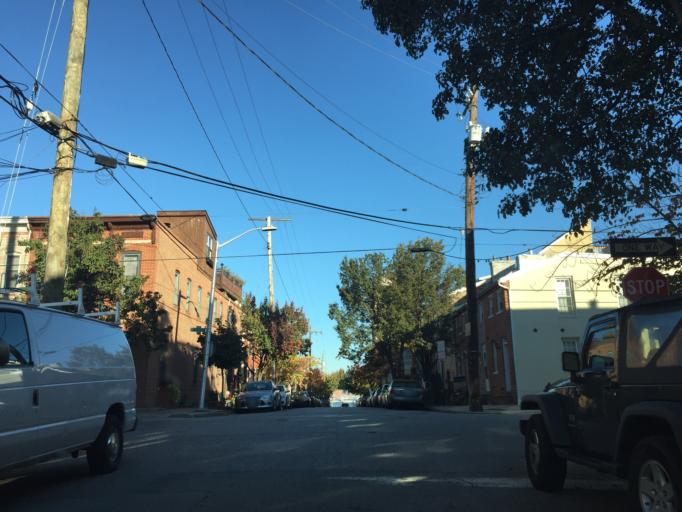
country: US
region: Maryland
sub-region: City of Baltimore
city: Baltimore
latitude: 39.2774
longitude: -76.6093
